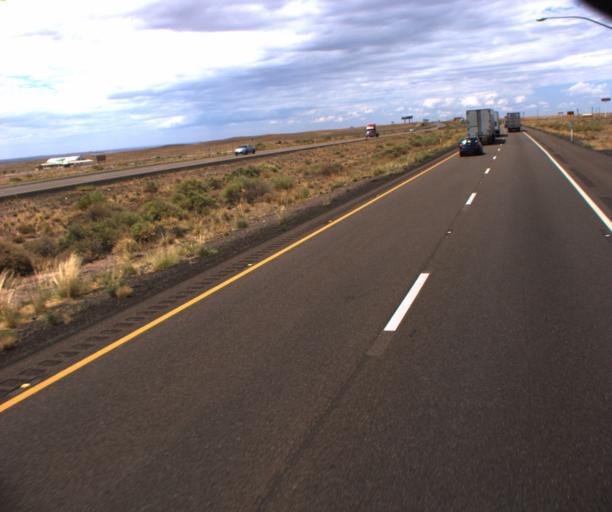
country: US
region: Arizona
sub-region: Navajo County
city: Holbrook
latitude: 34.9750
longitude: -110.0832
